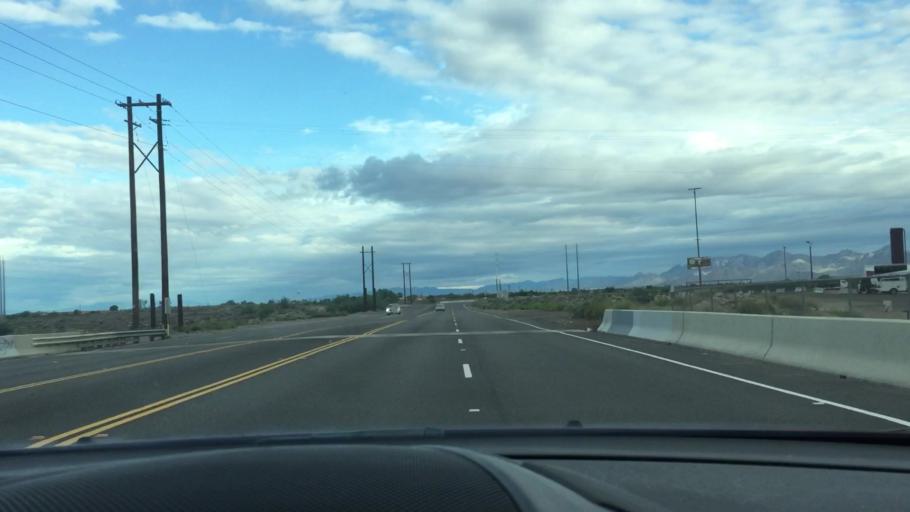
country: US
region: Arizona
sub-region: Maricopa County
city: Mesa
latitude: 33.4485
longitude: -111.8567
